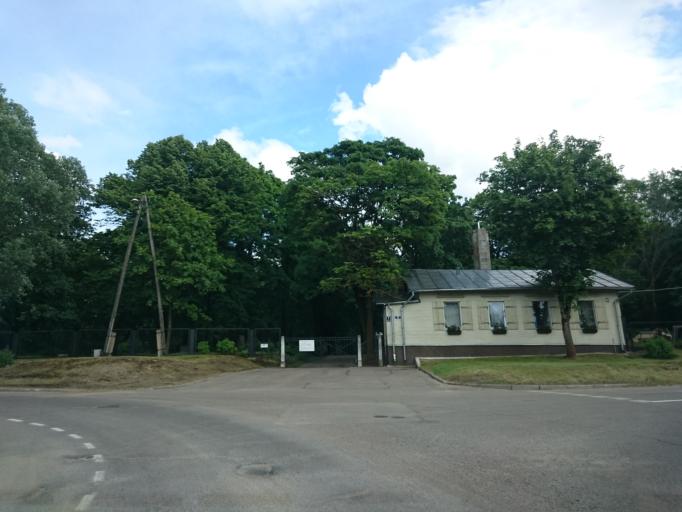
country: LV
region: Riga
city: Riga
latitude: 56.9471
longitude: 24.1545
